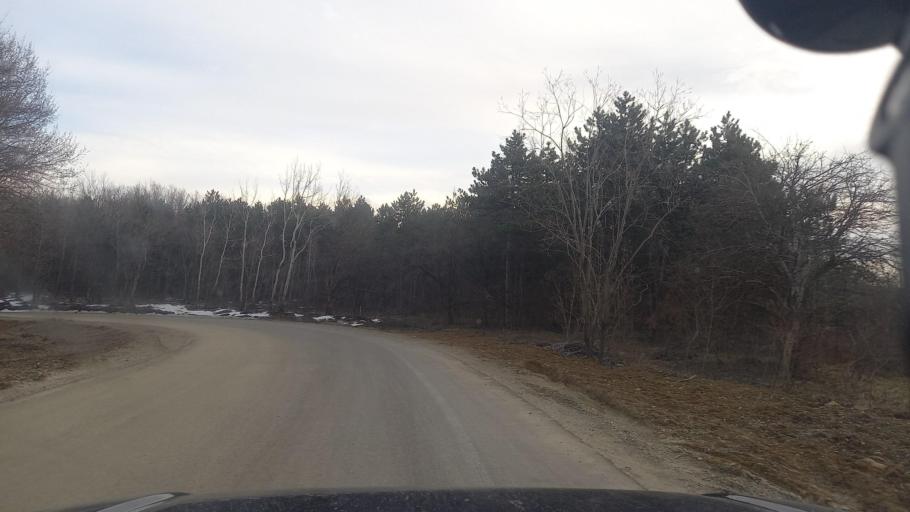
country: RU
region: Krasnodarskiy
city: Goryachiy Klyuch
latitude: 44.6985
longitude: 38.9863
